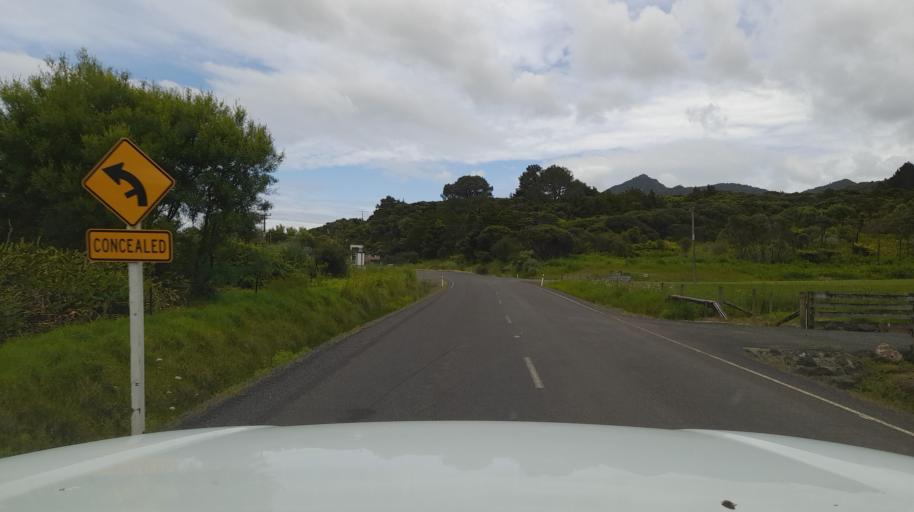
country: NZ
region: Northland
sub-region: Far North District
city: Kaitaia
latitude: -35.3885
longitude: 173.3826
